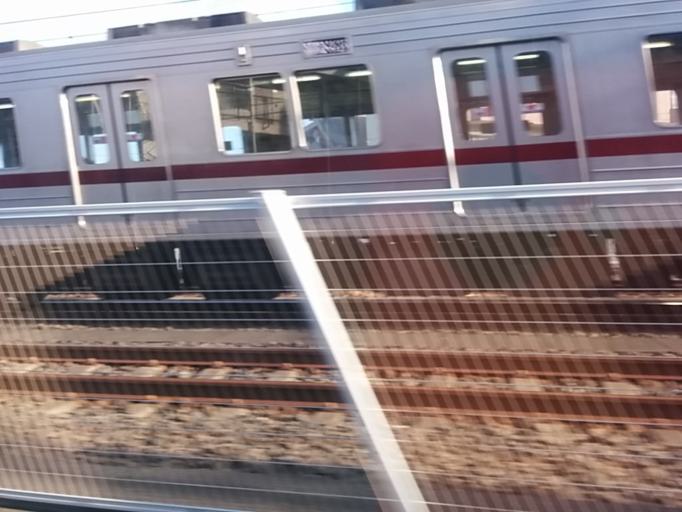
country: JP
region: Saitama
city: Shiki
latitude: 35.8246
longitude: 139.5712
